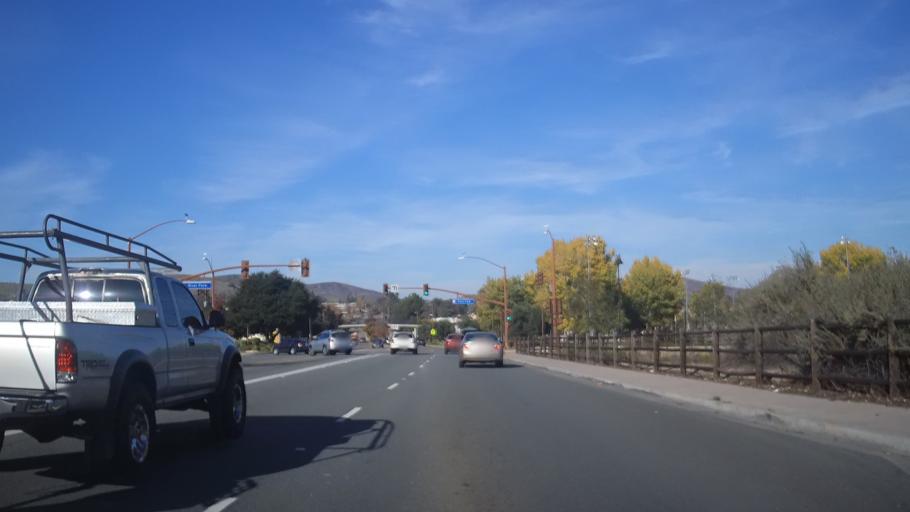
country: US
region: California
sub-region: San Diego County
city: Santee
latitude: 32.8469
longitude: -116.9834
